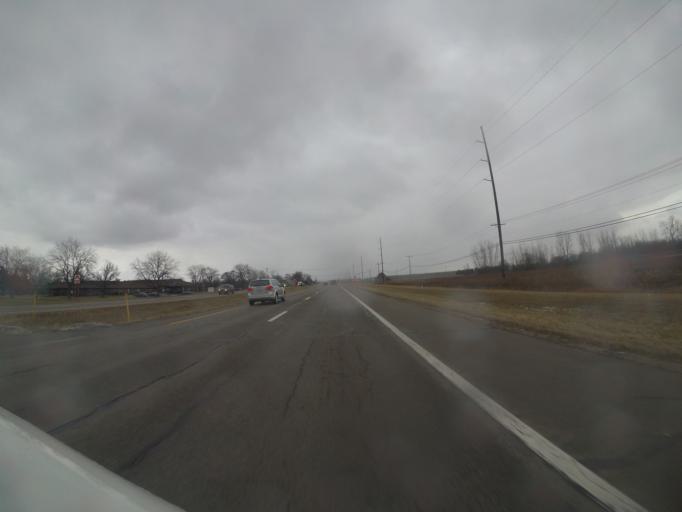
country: US
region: Ohio
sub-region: Wood County
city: Walbridge
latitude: 41.5637
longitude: -83.5352
